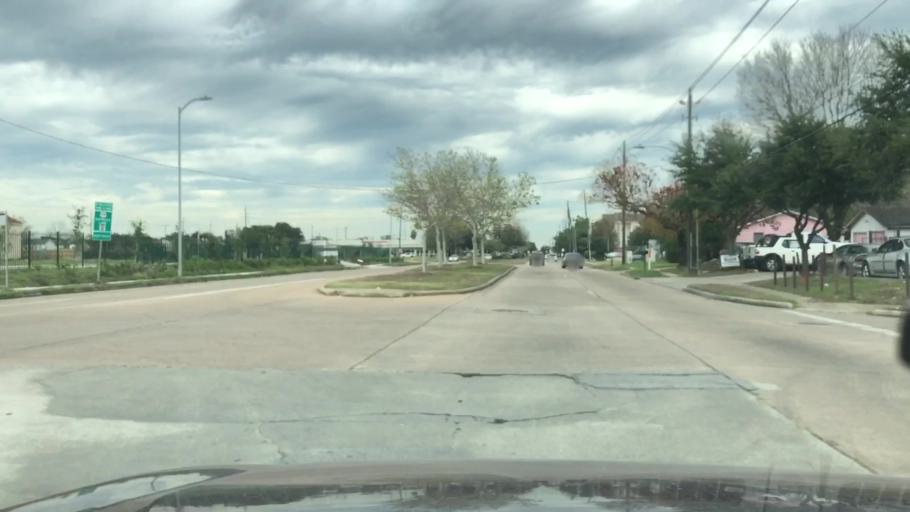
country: US
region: Texas
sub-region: Fort Bend County
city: Missouri City
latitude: 29.6581
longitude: -95.5279
